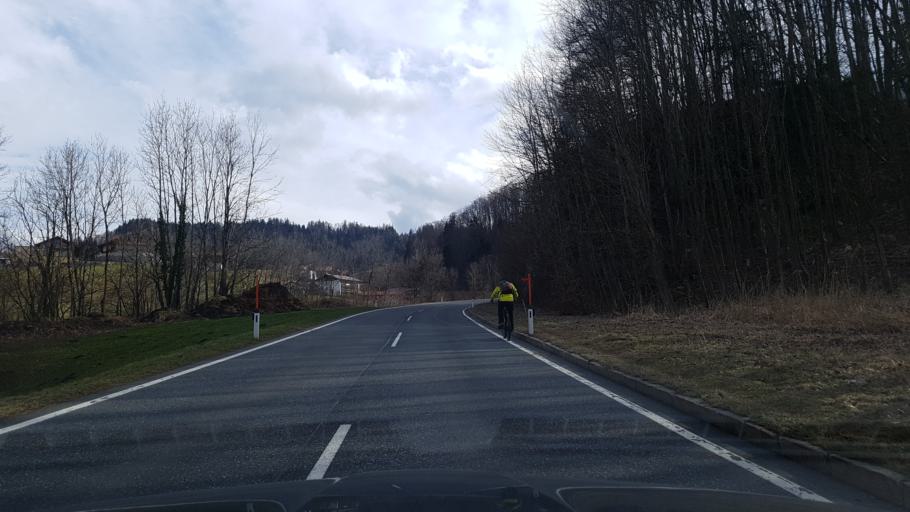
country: AT
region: Salzburg
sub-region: Politischer Bezirk Hallein
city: Hallein
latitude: 47.6653
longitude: 13.0942
